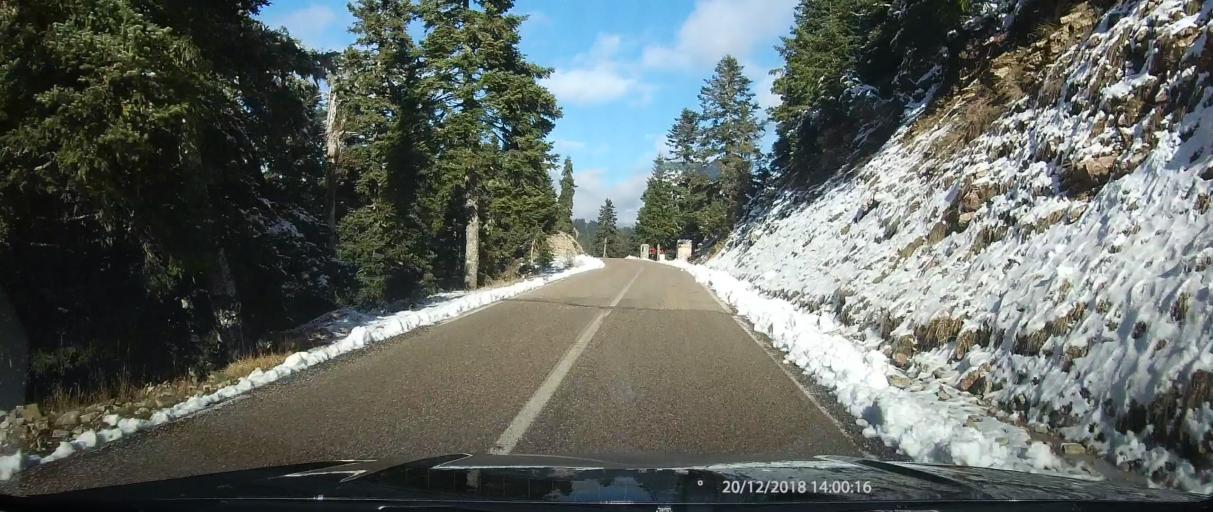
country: GR
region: West Greece
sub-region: Nomos Aitolias kai Akarnanias
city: Thermo
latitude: 38.7237
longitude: 21.6271
